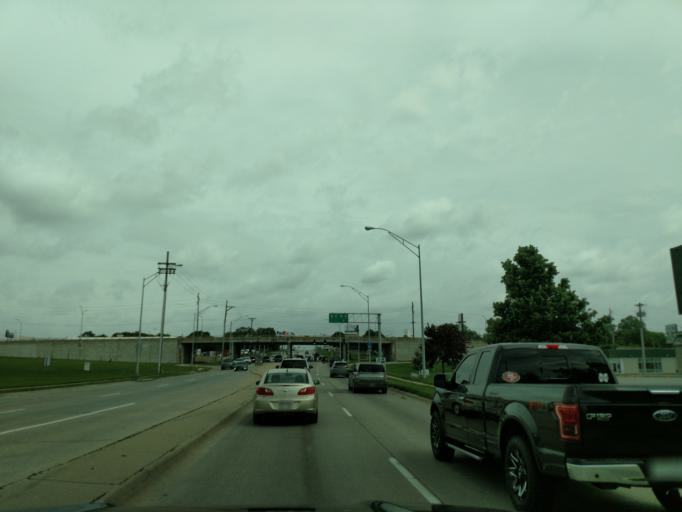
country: US
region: Nebraska
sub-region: Douglas County
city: Ralston
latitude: 41.2110
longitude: -96.0238
